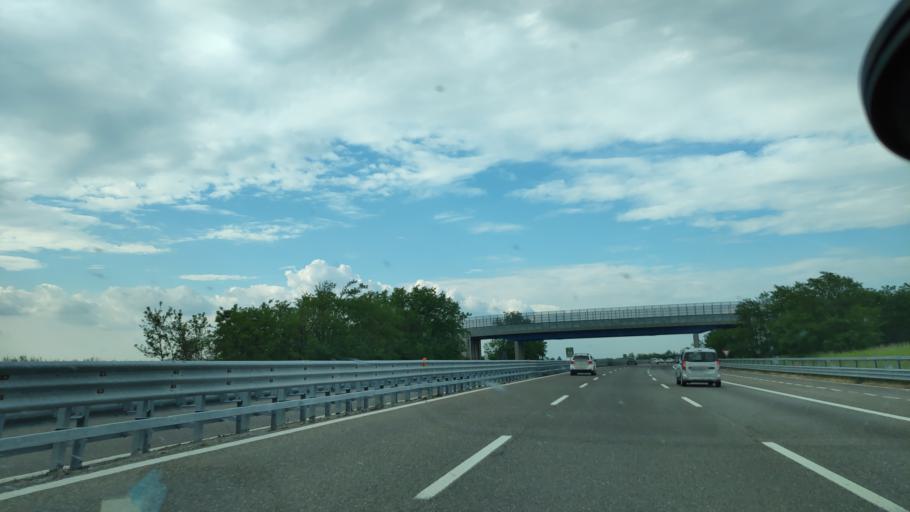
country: IT
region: Lombardy
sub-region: Provincia di Pavia
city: Pieve Albignola
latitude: 45.1252
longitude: 8.9780
